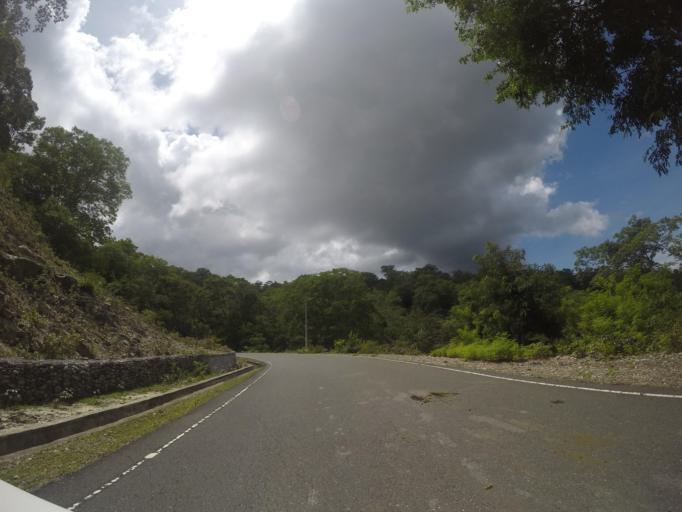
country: TL
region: Bobonaro
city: Maliana
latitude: -8.9538
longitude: 125.0914
